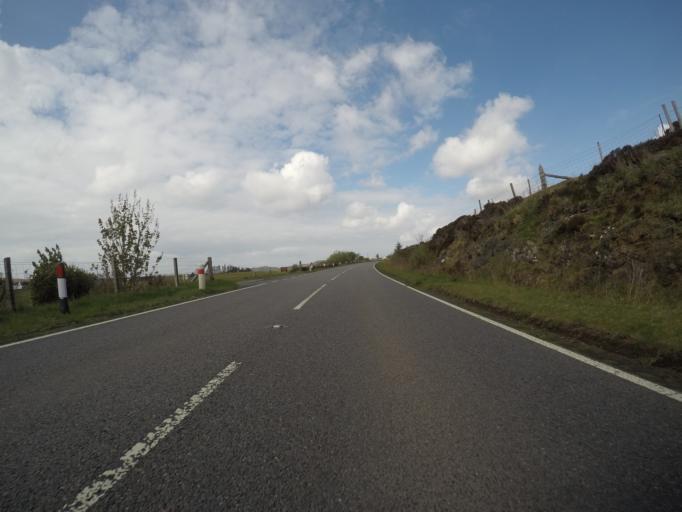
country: GB
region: Scotland
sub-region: Highland
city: Portree
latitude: 57.5620
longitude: -6.3642
